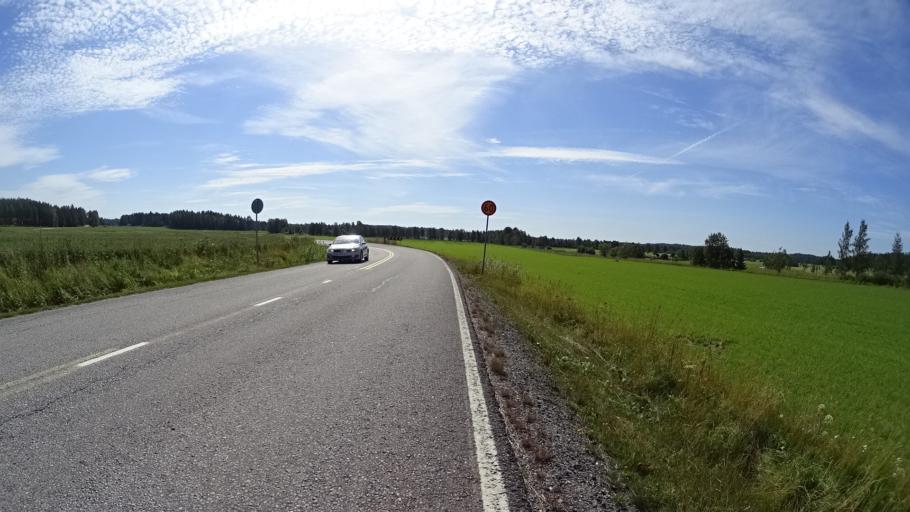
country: FI
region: Uusimaa
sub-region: Helsinki
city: Kirkkonummi
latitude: 60.1016
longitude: 24.4870
